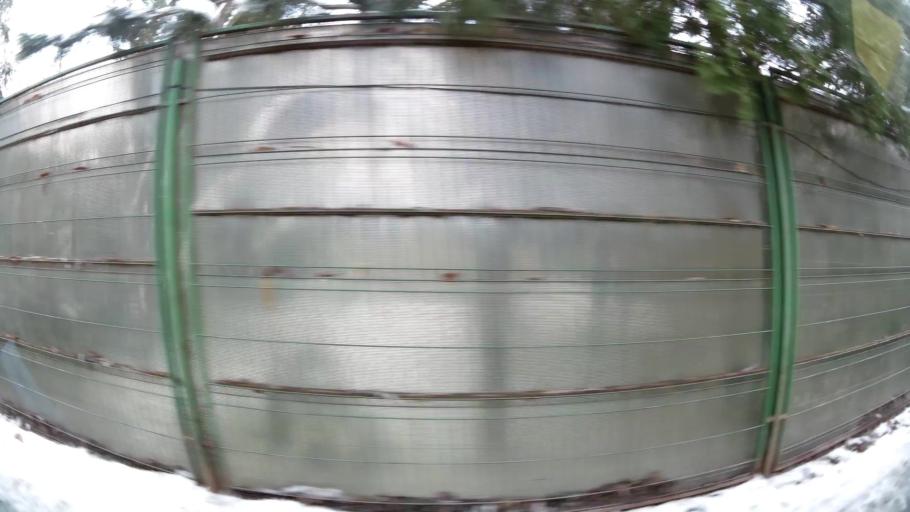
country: RO
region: Ilfov
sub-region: Comuna Tunari
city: Tunari
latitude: 44.5133
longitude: 26.1143
